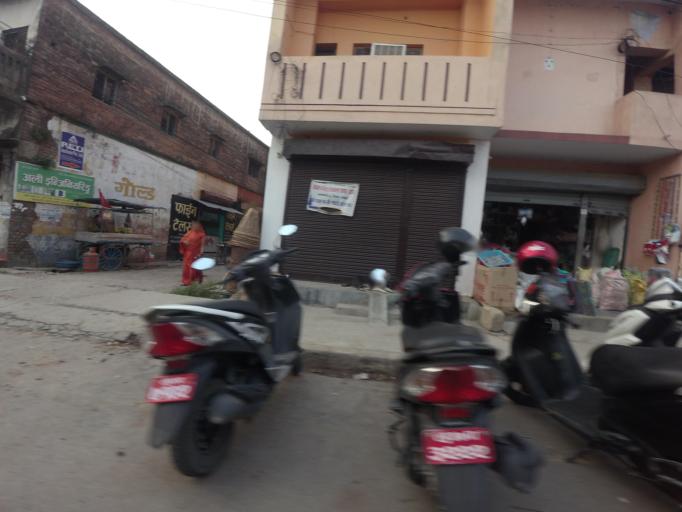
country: NP
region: Western Region
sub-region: Lumbini Zone
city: Bhairahawa
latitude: 27.5067
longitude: 83.4495
